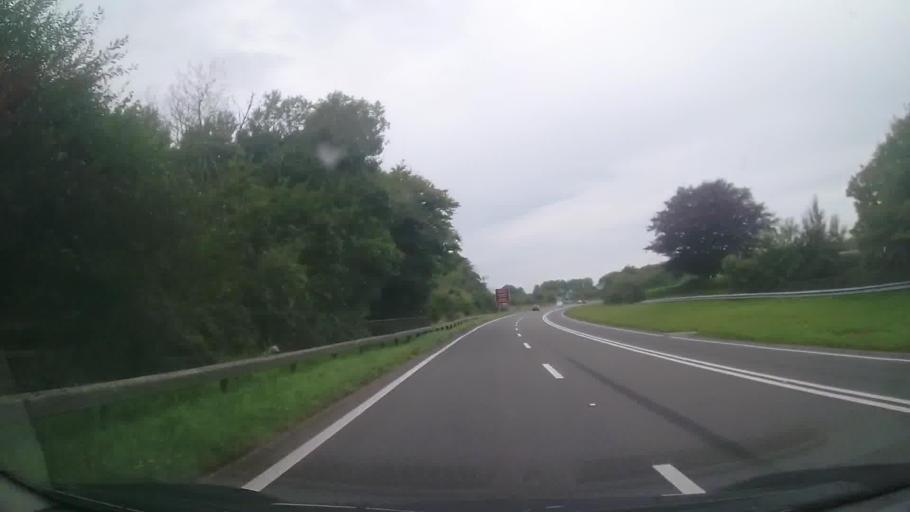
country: GB
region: Wales
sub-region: Pembrokeshire
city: Kilgetty
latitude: 51.7283
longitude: -4.7139
